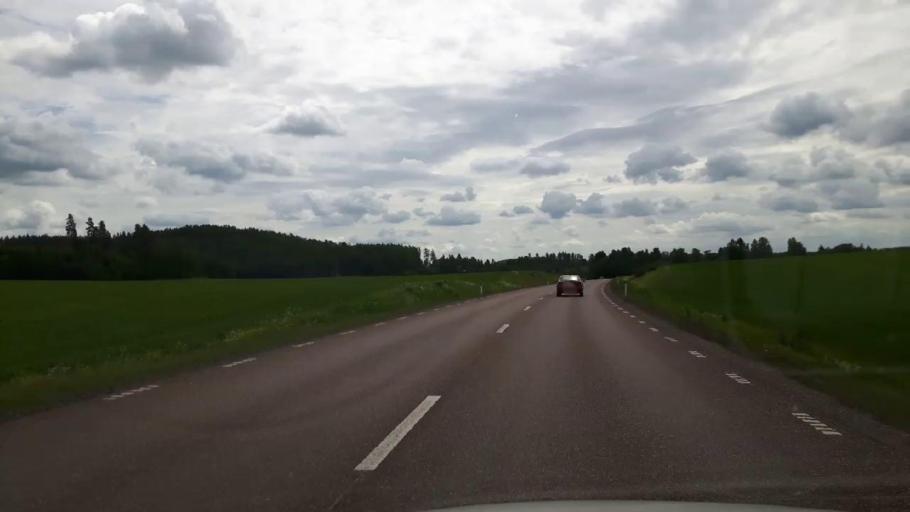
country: SE
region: Dalarna
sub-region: Hedemora Kommun
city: Hedemora
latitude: 60.3297
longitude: 15.9495
